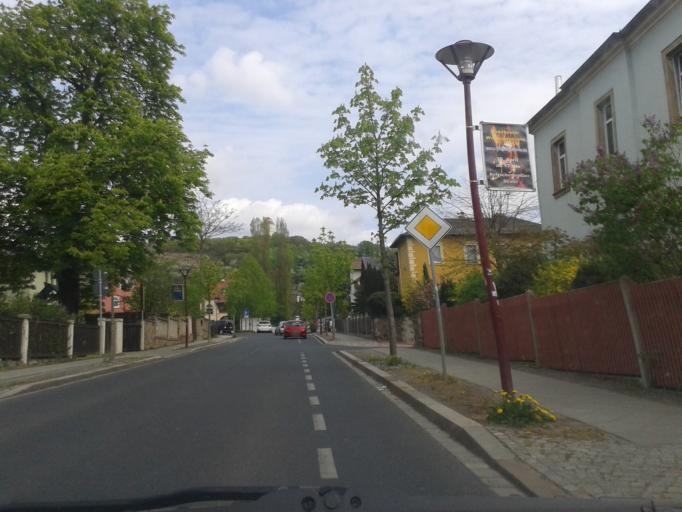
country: DE
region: Saxony
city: Radebeul
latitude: 51.1114
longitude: 13.6326
